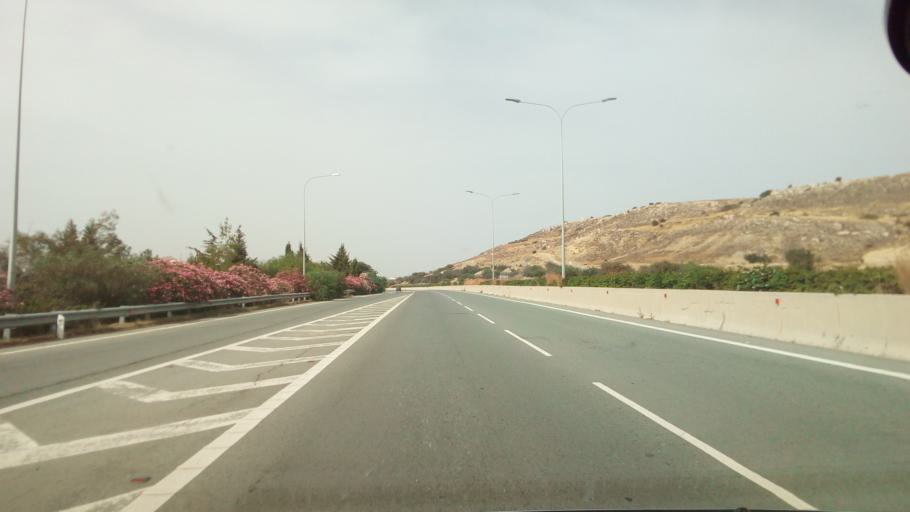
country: CY
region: Larnaka
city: Pyla
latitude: 34.9947
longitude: 33.6980
